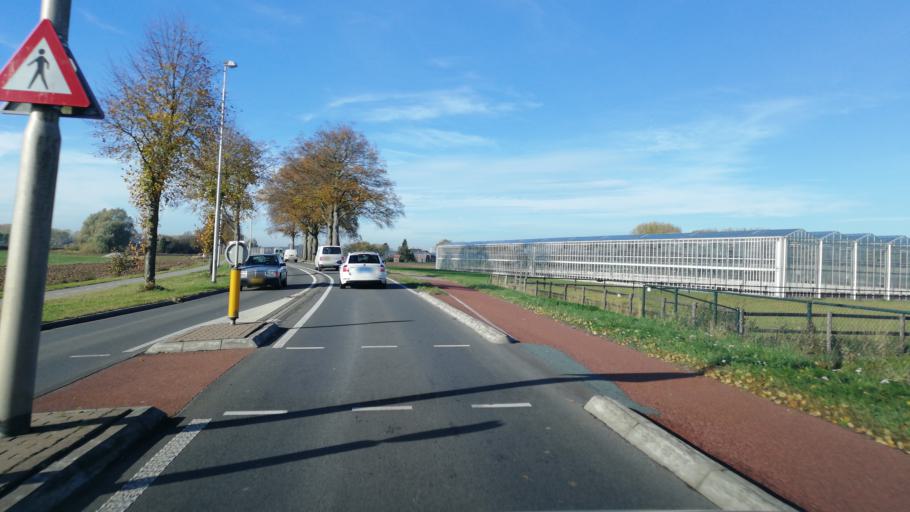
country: NL
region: Gelderland
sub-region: Gemeente Zutphen
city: Zutphen
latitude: 52.1460
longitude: 6.1701
